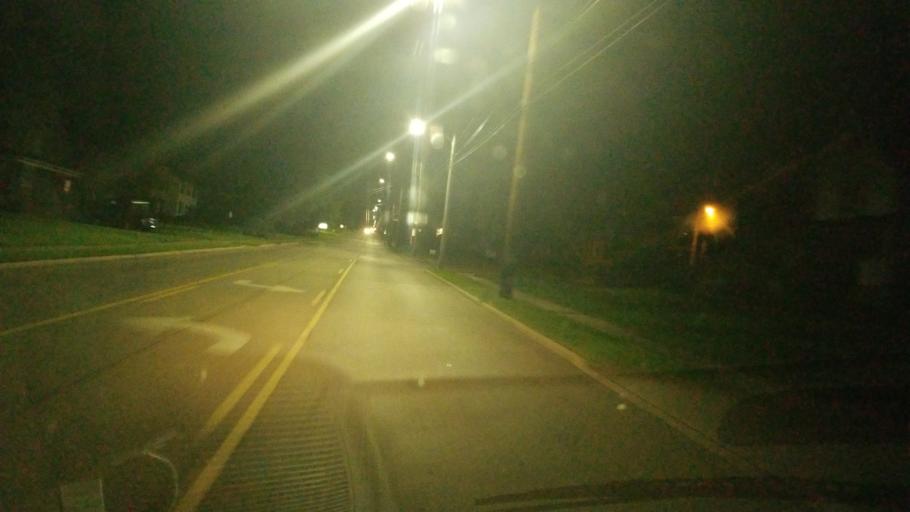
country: US
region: Ohio
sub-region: Trumbull County
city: Niles
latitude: 41.1825
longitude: -80.7495
